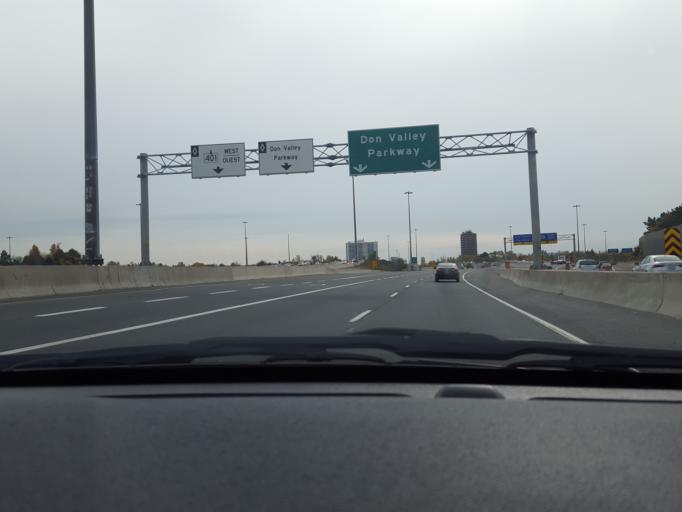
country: CA
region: Ontario
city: Willowdale
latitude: 43.7722
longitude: -79.3392
